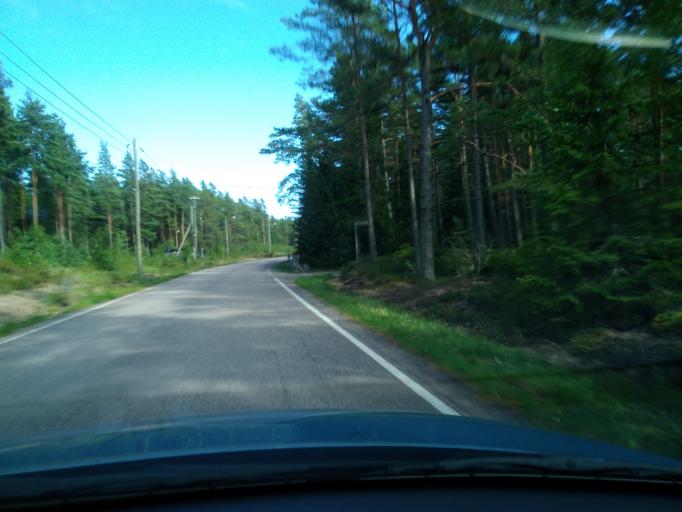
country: FI
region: Uusimaa
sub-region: Raaseporin
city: Hanko
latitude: 59.8405
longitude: 23.0856
